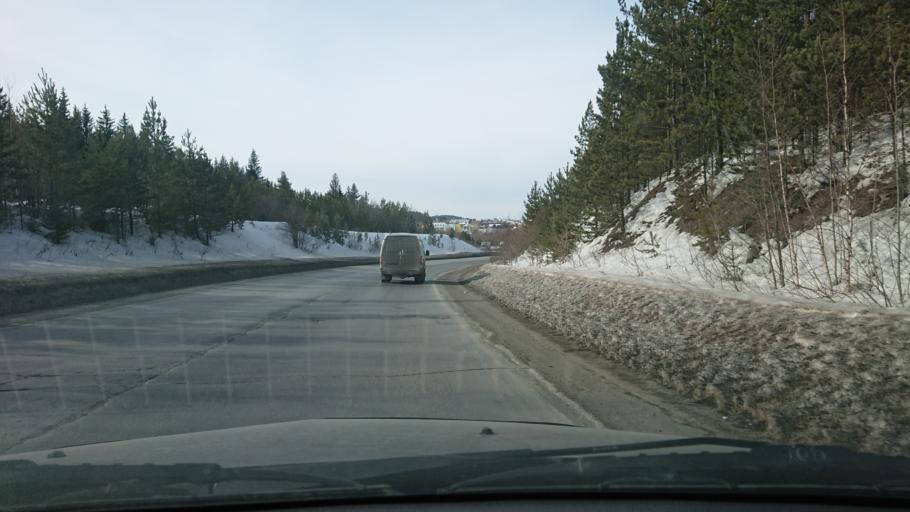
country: RU
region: Sverdlovsk
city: Revda
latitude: 56.7966
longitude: 59.9885
